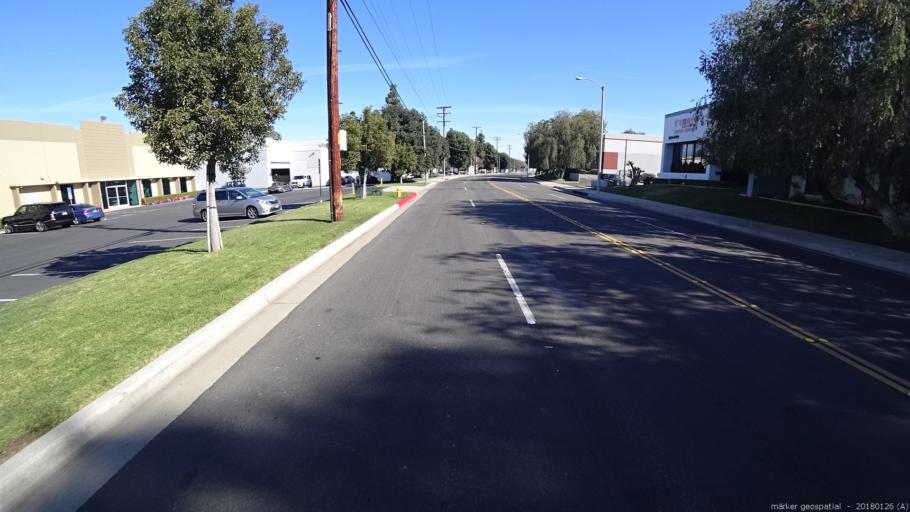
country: US
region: California
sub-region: Los Angeles County
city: Walnut
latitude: 34.0008
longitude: -117.8577
